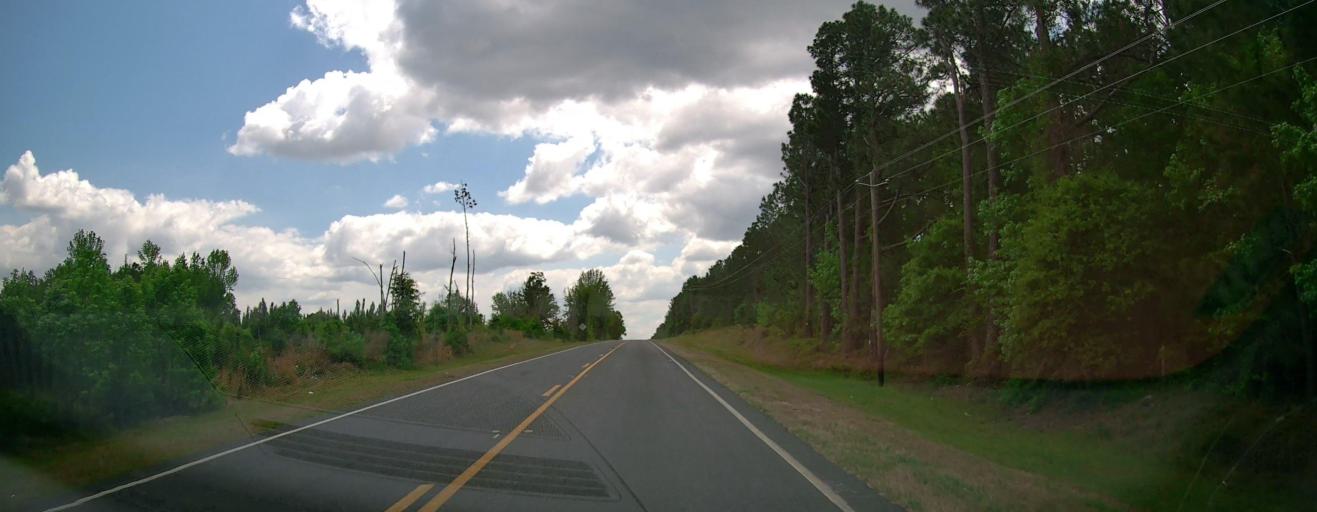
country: US
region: Georgia
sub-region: Treutlen County
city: Soperton
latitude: 32.4676
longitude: -82.6025
